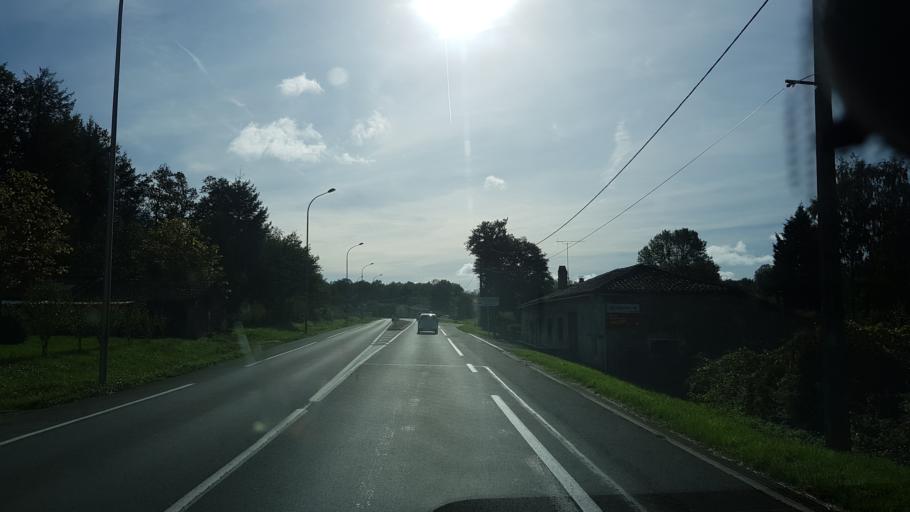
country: FR
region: Poitou-Charentes
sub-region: Departement de la Charente
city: Loubert
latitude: 45.9382
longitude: 0.5381
